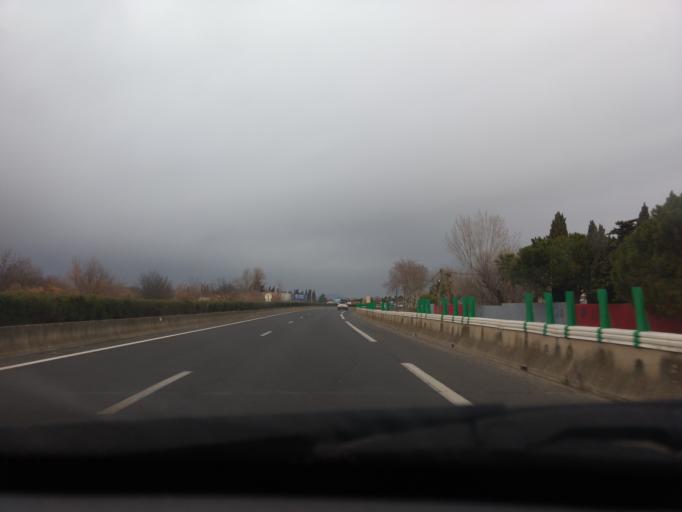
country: FR
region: Languedoc-Roussillon
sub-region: Departement de l'Herault
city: Lattes
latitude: 43.5502
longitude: 3.8938
